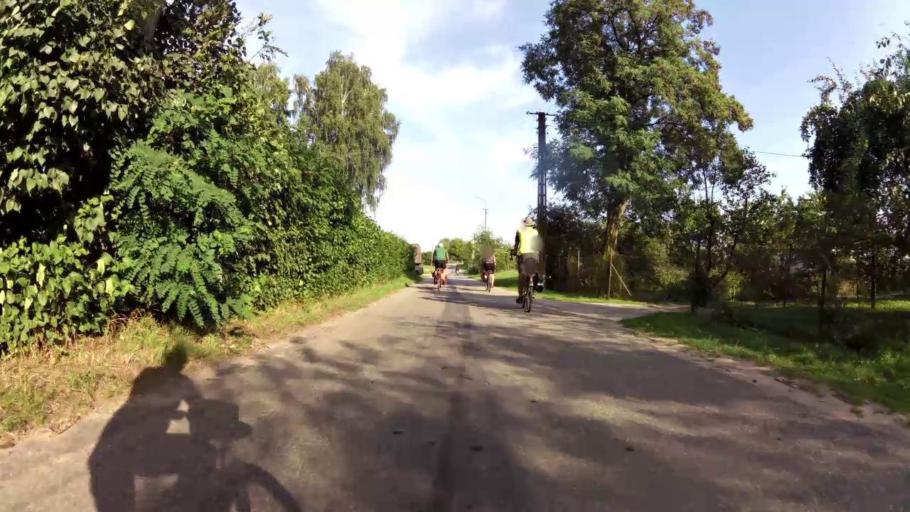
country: PL
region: West Pomeranian Voivodeship
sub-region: Powiat drawski
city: Drawsko Pomorskie
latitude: 53.4929
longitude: 15.7837
